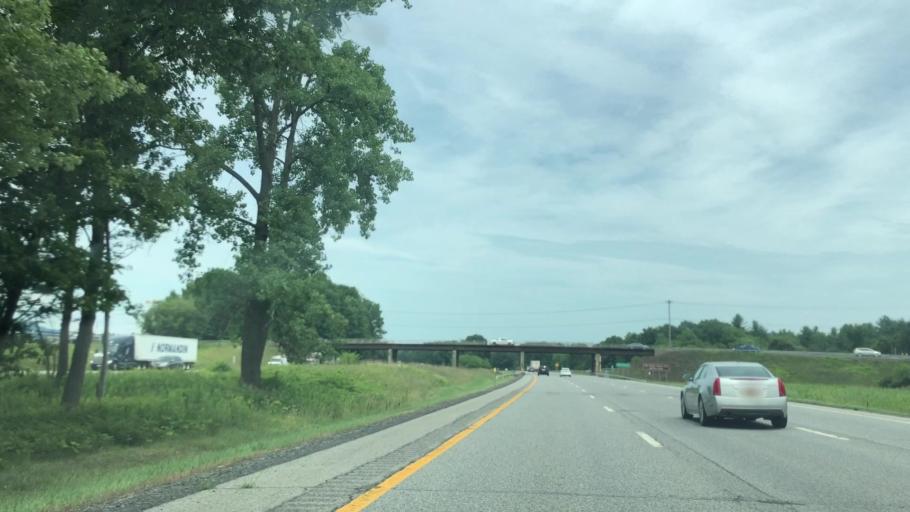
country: US
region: New York
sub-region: Saratoga County
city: Saratoga Springs
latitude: 43.1677
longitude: -73.7134
